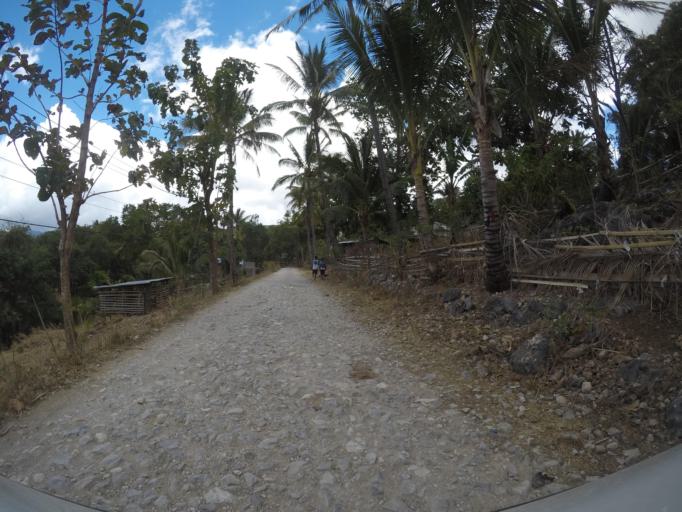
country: TL
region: Baucau
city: Baucau
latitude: -8.5217
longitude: 126.6949
